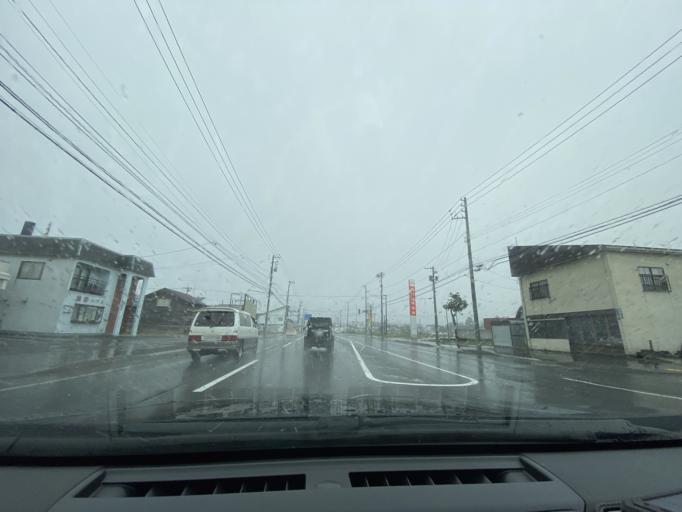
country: JP
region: Hokkaido
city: Takikawa
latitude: 43.6229
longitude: 141.9399
